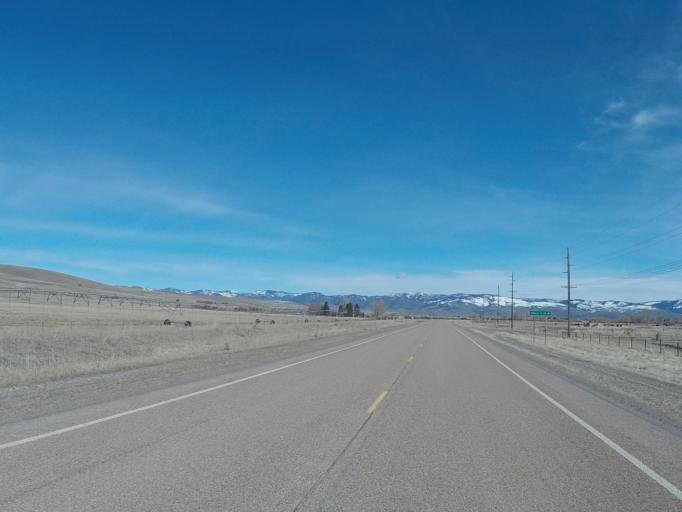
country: US
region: Montana
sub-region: Granite County
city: Philipsburg
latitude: 46.5499
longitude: -113.2182
